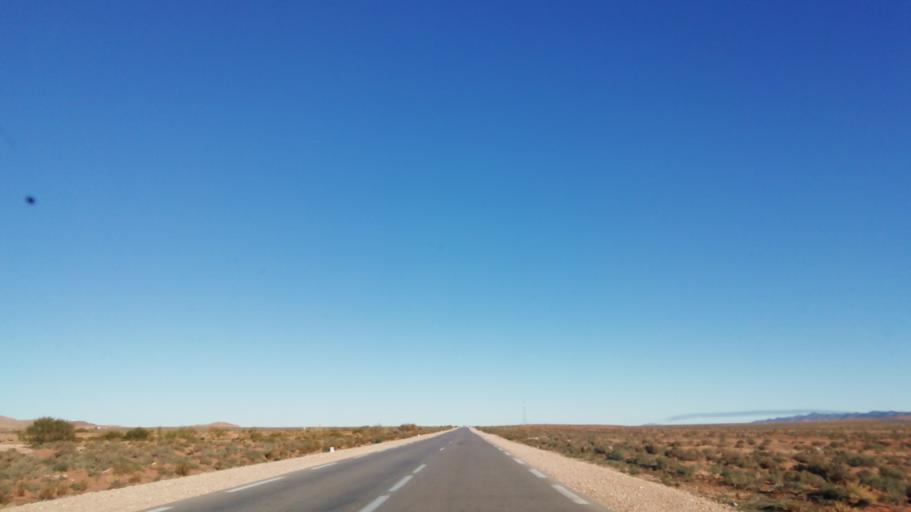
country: DZ
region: El Bayadh
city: El Abiodh Sidi Cheikh
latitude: 33.1118
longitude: 0.2276
